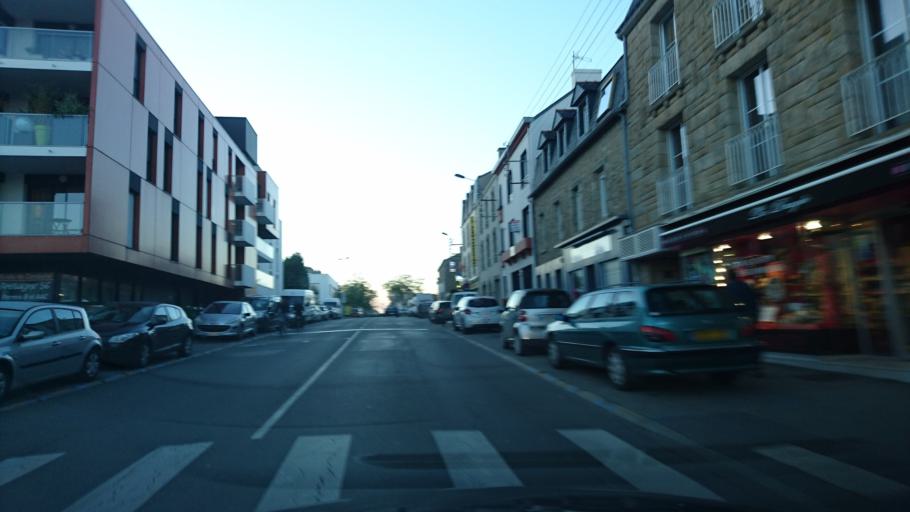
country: FR
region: Brittany
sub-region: Departement du Morbihan
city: Auray
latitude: 47.6697
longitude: -2.9887
